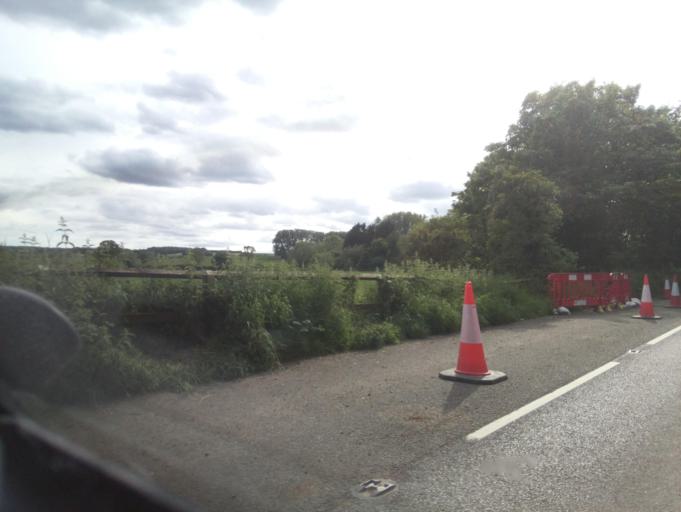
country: GB
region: England
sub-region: Gloucestershire
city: Chipping Campden
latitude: 52.0524
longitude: -1.7597
